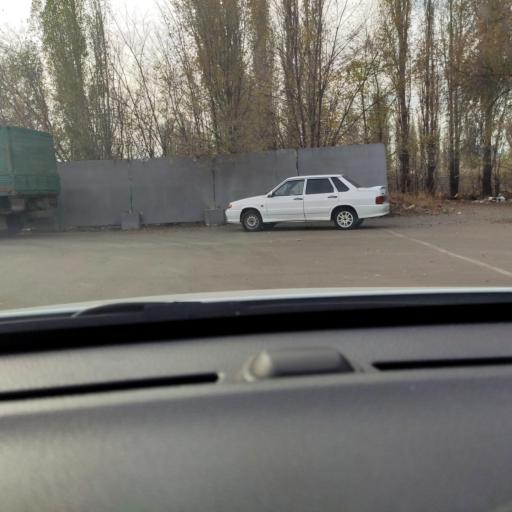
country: RU
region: Voronezj
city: Novaya Usman'
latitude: 51.6504
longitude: 39.4213
